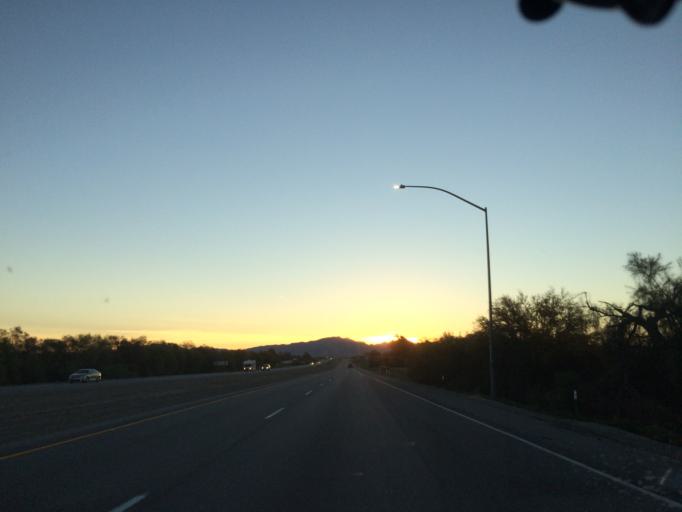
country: US
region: California
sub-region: Riverside County
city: Blythe
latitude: 33.6070
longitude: -114.5838
